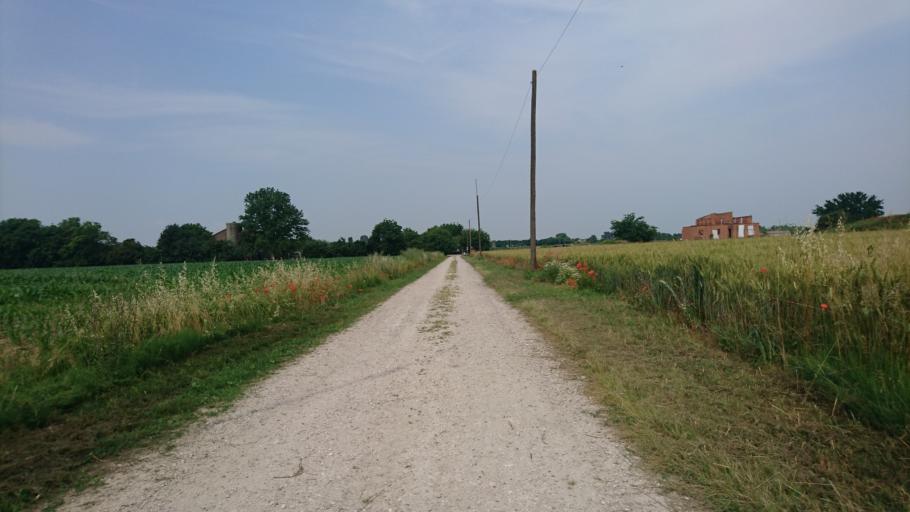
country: IT
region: Veneto
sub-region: Provincia di Padova
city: Polverara
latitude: 45.3253
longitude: 11.9518
